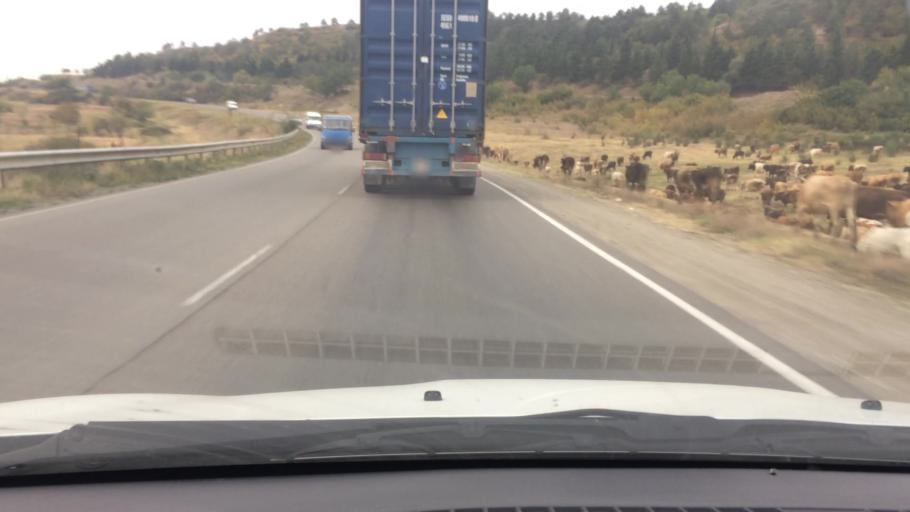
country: GE
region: T'bilisi
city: Tbilisi
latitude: 41.6018
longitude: 44.7788
